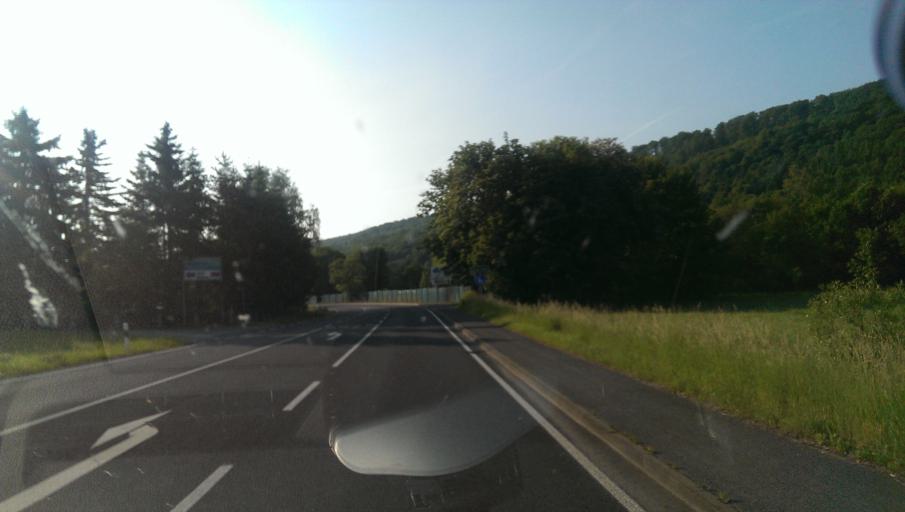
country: DE
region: Thuringia
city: Rohr
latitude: 50.5727
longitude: 10.5109
